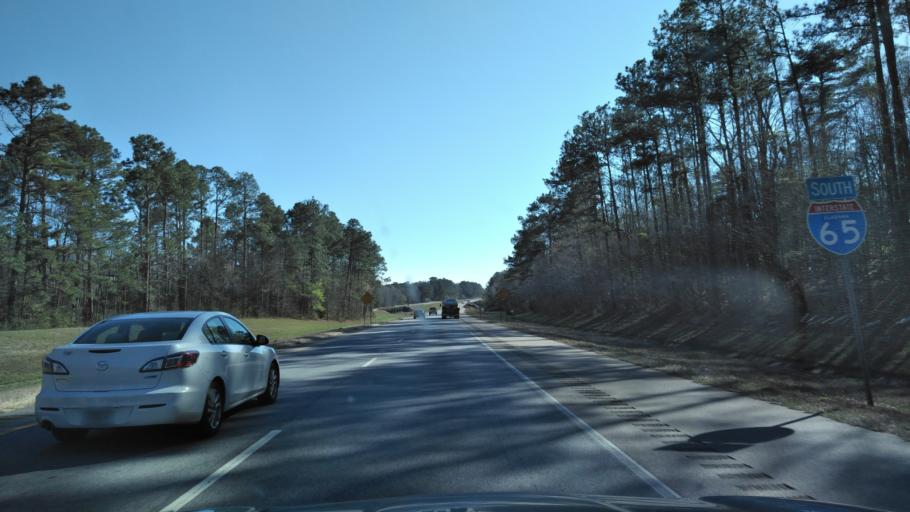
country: US
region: Alabama
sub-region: Butler County
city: Greenville
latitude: 31.8155
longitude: -86.6663
